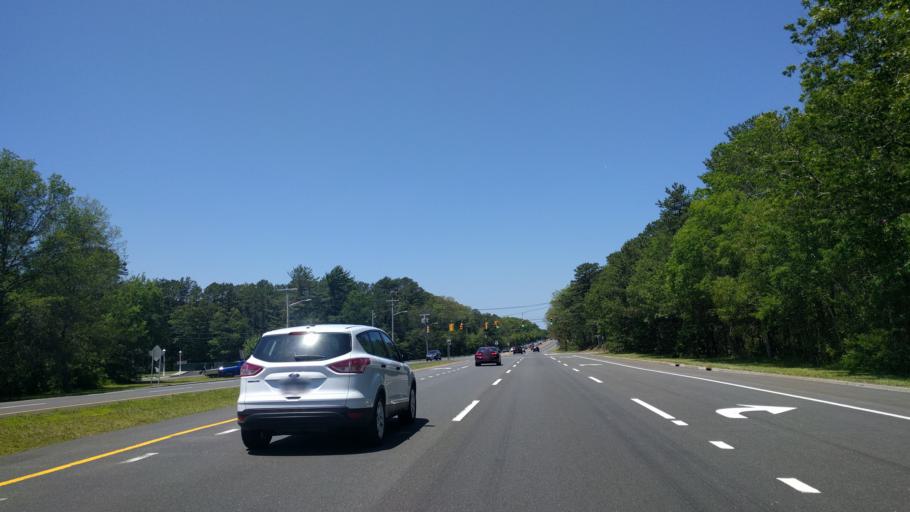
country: US
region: New York
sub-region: Suffolk County
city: Manorville
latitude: 40.8641
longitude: -72.7780
